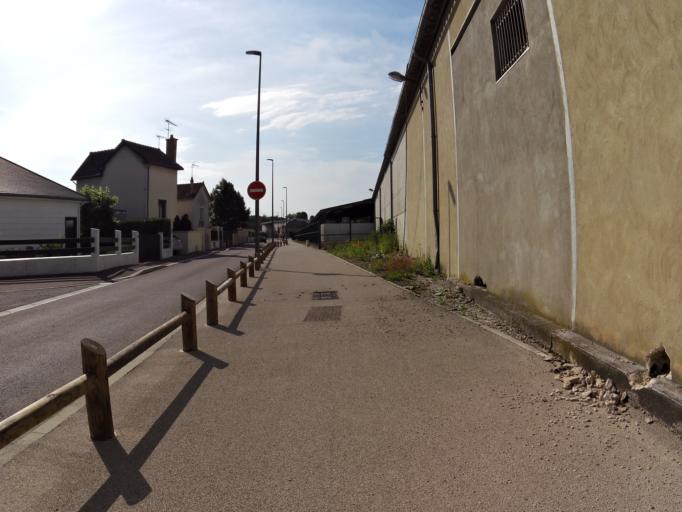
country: FR
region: Champagne-Ardenne
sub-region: Departement de l'Aube
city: Saint-Julien-les-Villas
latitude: 48.2846
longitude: 4.0909
